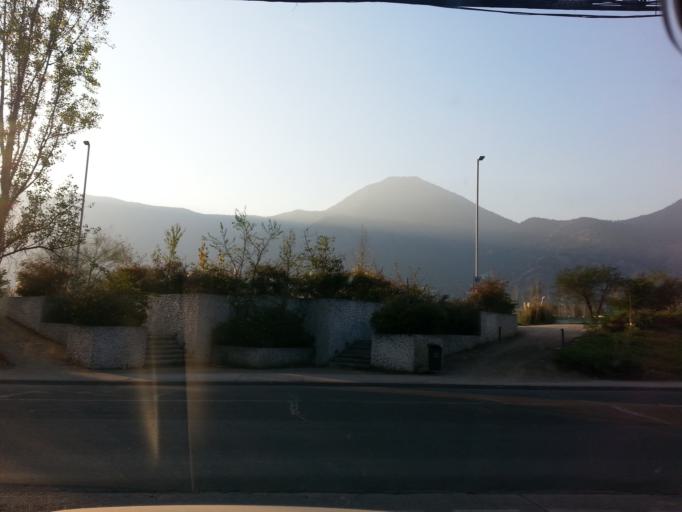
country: CL
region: Santiago Metropolitan
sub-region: Provincia de Santiago
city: Villa Presidente Frei, Nunoa, Santiago, Chile
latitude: -33.3806
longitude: -70.5744
